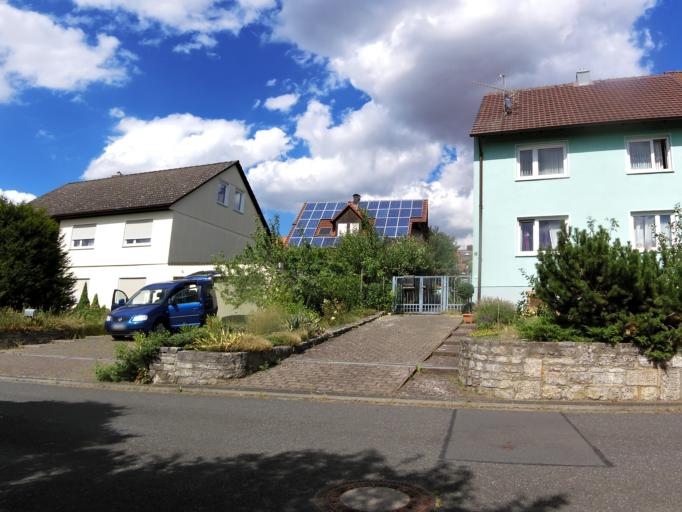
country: DE
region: Bavaria
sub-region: Regierungsbezirk Unterfranken
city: Eibelstadt
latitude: 49.7261
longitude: 10.0054
